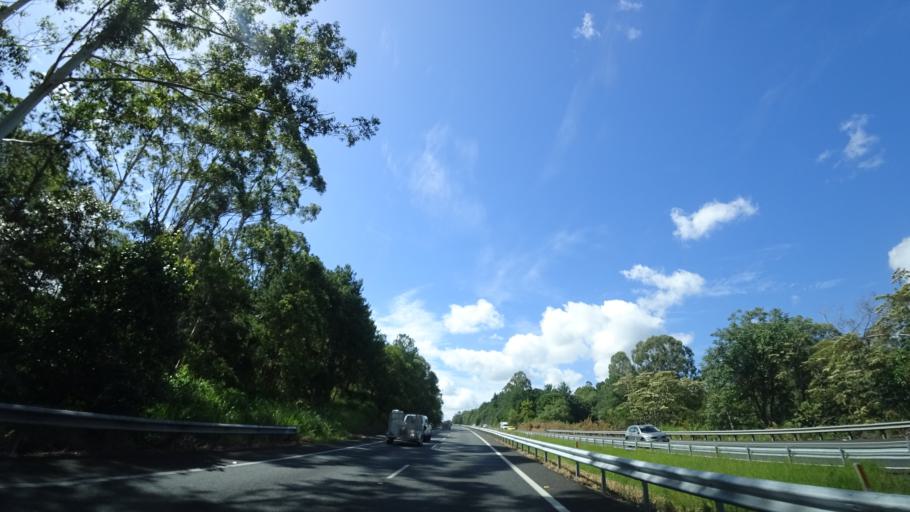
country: AU
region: Queensland
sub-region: Sunshine Coast
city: Woombye
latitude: -26.6628
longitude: 152.9959
